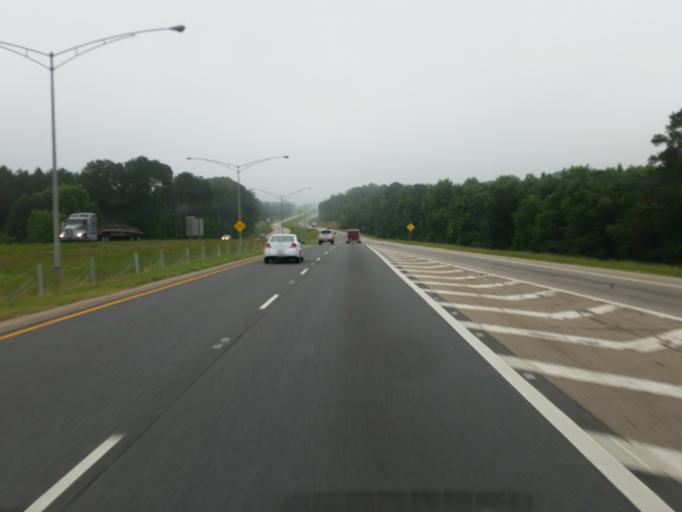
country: US
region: Louisiana
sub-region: Webster Parish
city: Minden
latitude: 32.5888
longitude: -93.2905
